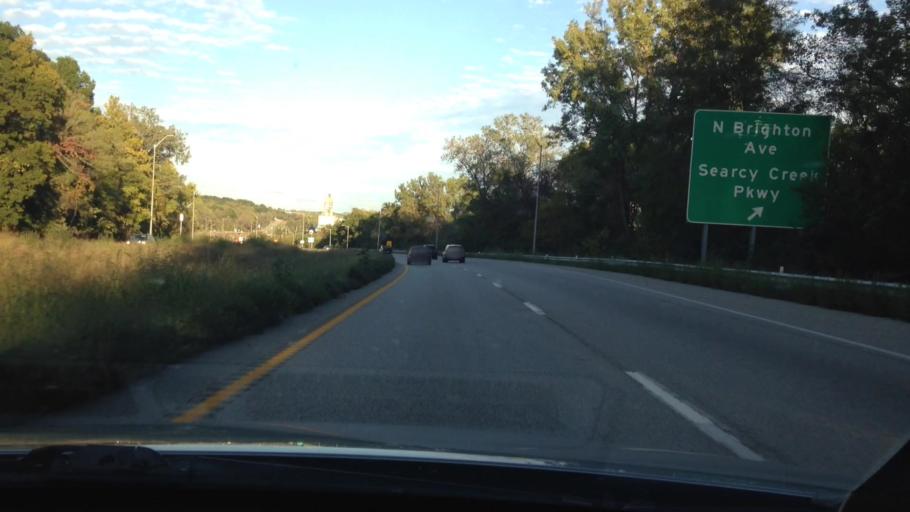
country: US
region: Missouri
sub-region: Clay County
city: North Kansas City
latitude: 39.1513
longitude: -94.5287
